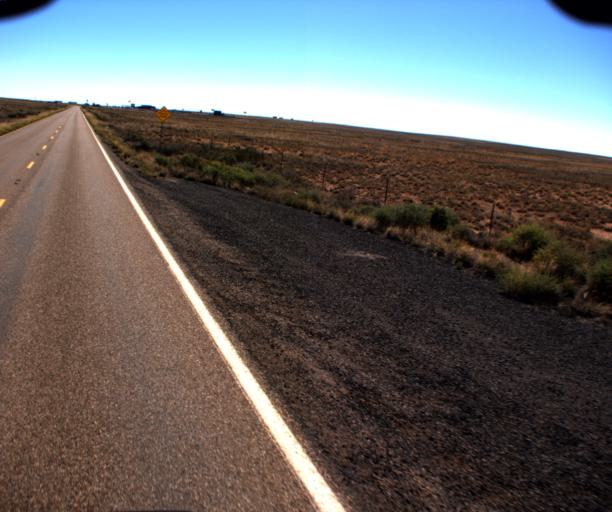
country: US
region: Arizona
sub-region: Navajo County
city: Holbrook
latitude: 34.9883
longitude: -110.0890
